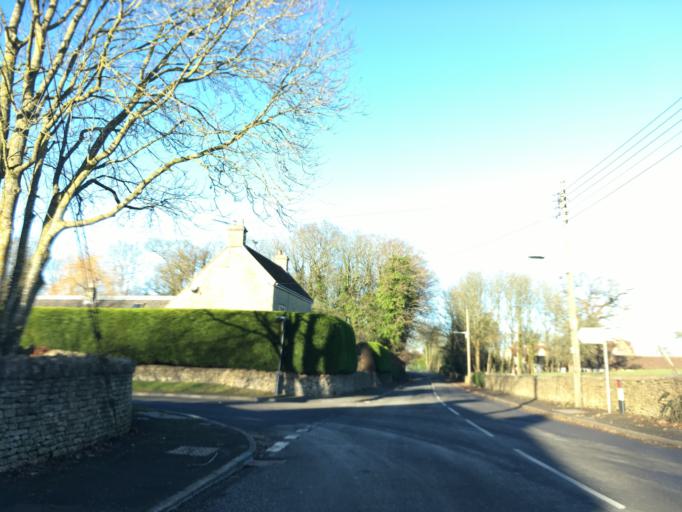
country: GB
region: England
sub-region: Wiltshire
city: Nettleton
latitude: 51.5283
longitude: -2.2768
